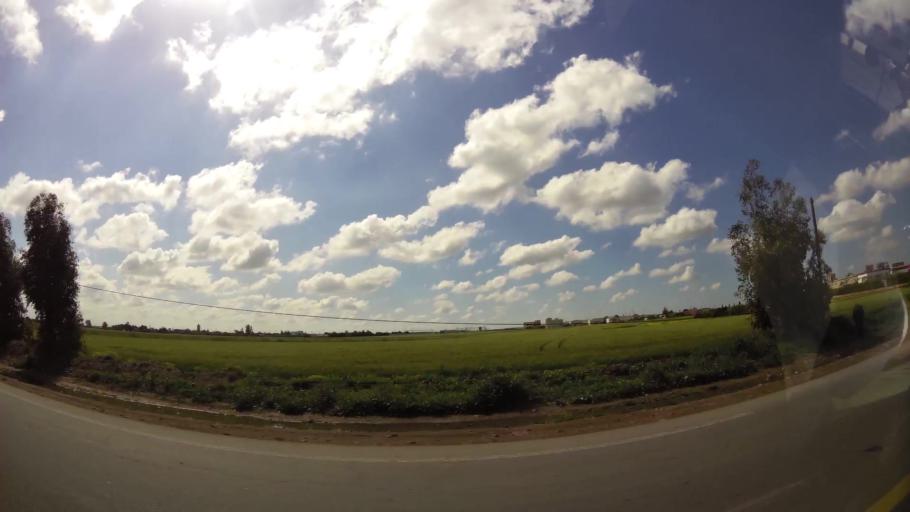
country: MA
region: Grand Casablanca
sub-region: Mediouna
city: Mediouna
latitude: 33.4296
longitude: -7.5227
